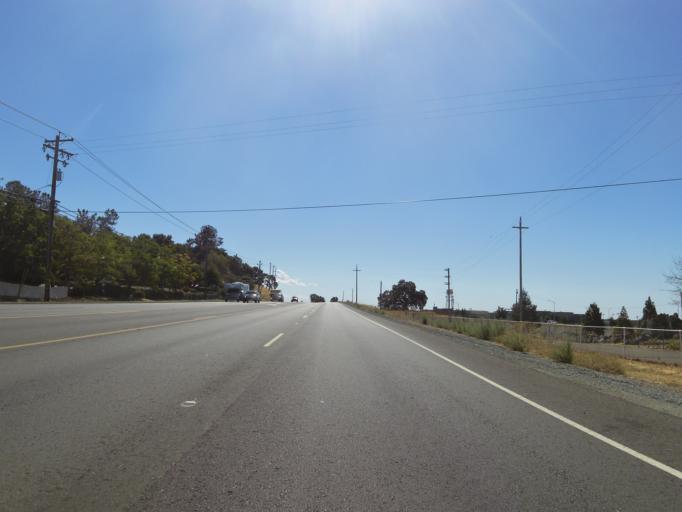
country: US
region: California
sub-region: Amador County
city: Sutter Creek
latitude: 38.3760
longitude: -120.8017
